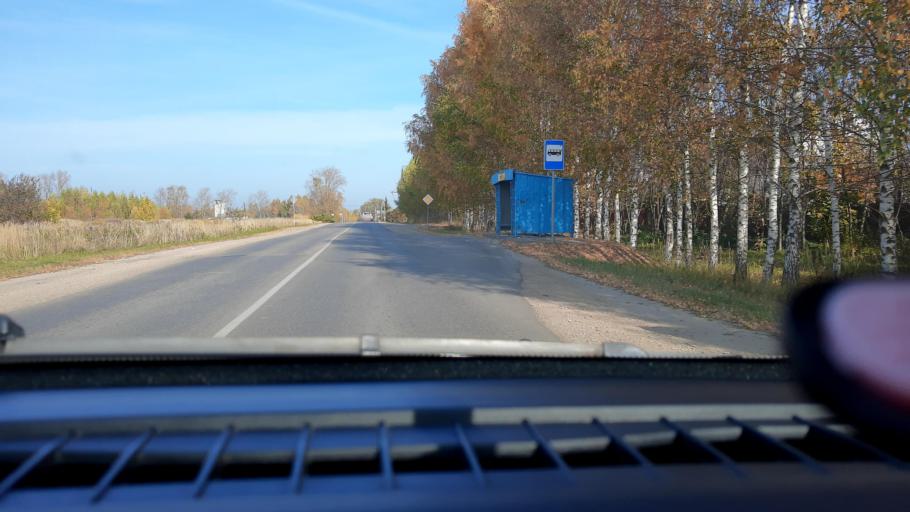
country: RU
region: Nizjnij Novgorod
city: Kstovo
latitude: 56.1490
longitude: 44.2313
